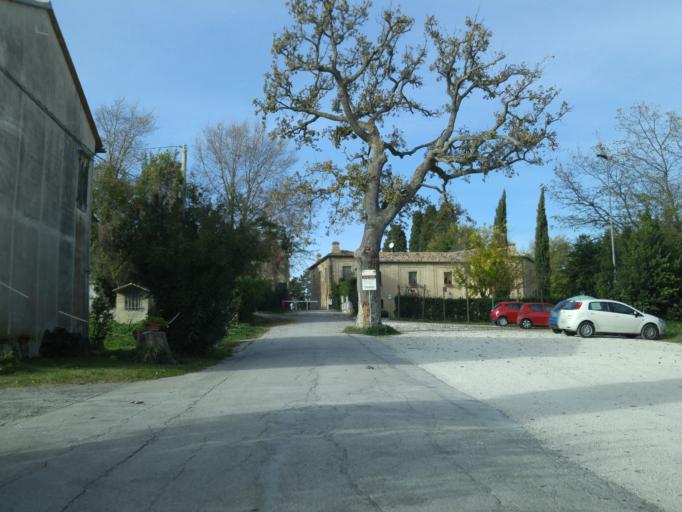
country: IT
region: The Marches
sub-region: Provincia di Pesaro e Urbino
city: Saltara
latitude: 43.7556
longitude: 12.8914
